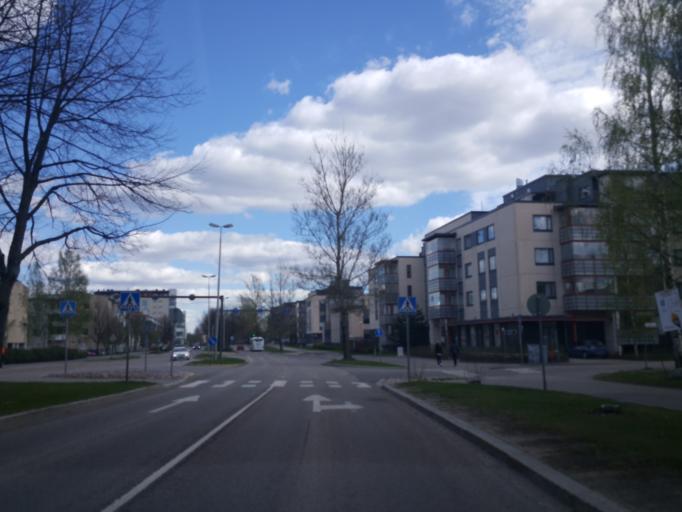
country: FI
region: Uusimaa
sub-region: Helsinki
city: Teekkarikylae
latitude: 60.2590
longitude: 24.8450
